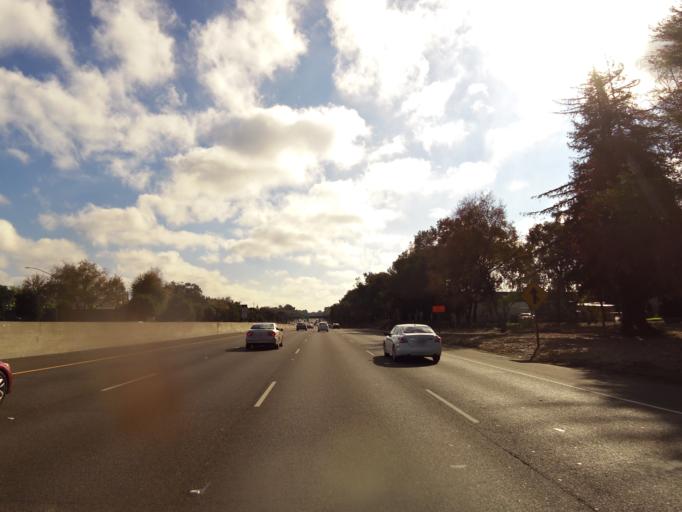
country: US
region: California
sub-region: Sacramento County
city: Parkway
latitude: 38.5243
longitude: -121.4675
